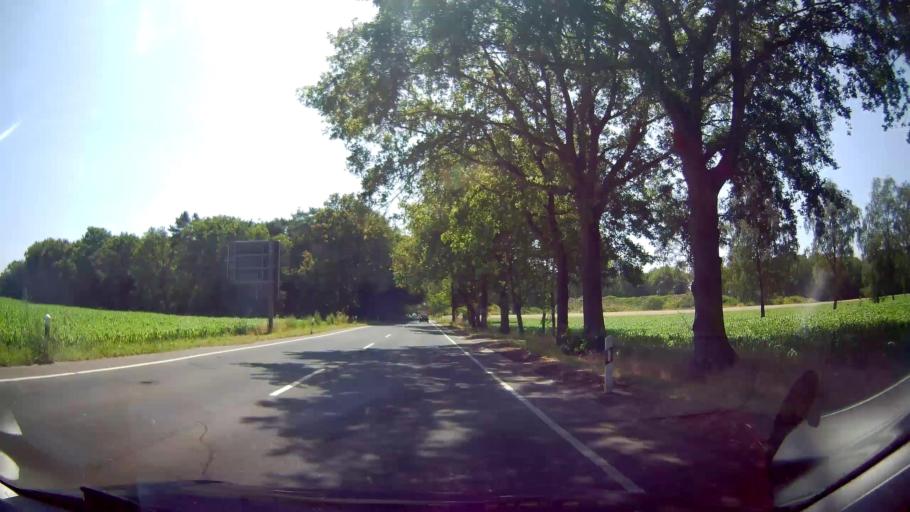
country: DE
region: North Rhine-Westphalia
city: Marl
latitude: 51.6523
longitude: 7.0391
